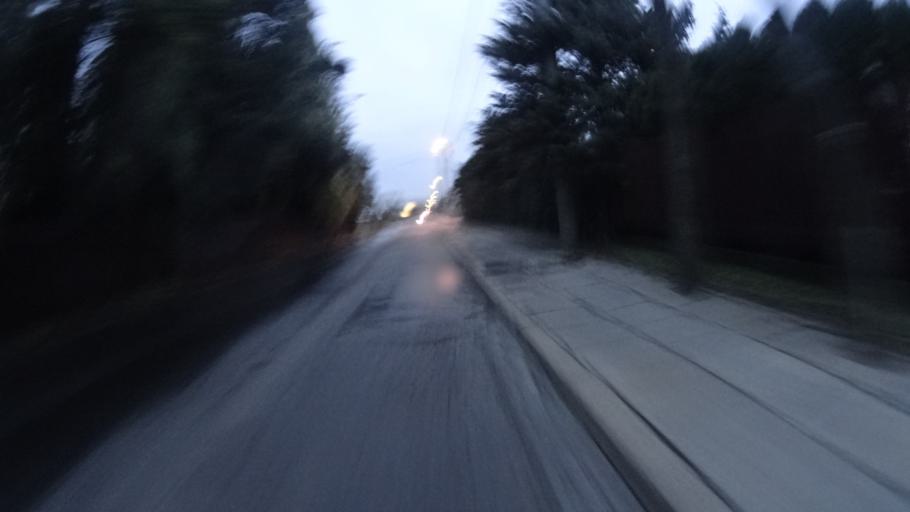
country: PL
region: Masovian Voivodeship
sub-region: Warszawa
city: Ursus
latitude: 52.2240
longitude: 20.8933
